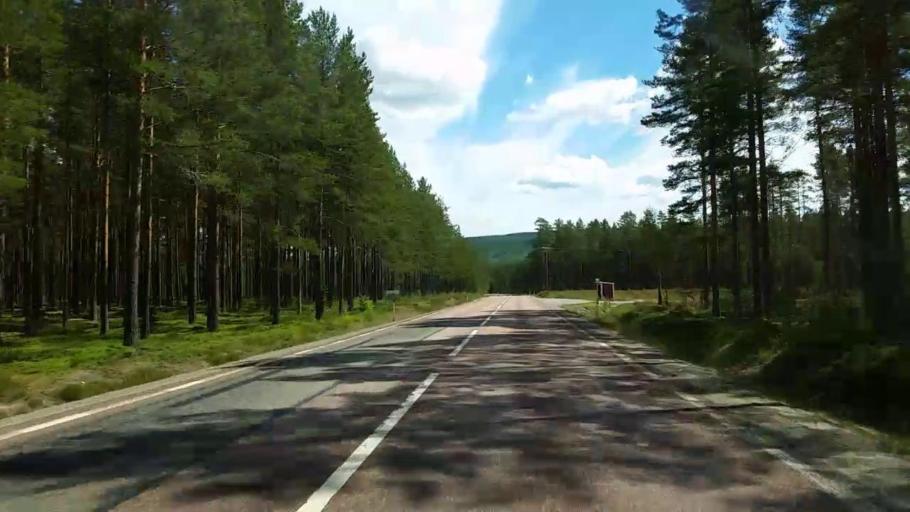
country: SE
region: Gaevleborg
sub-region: Ovanakers Kommun
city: Edsbyn
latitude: 61.3502
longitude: 15.5893
